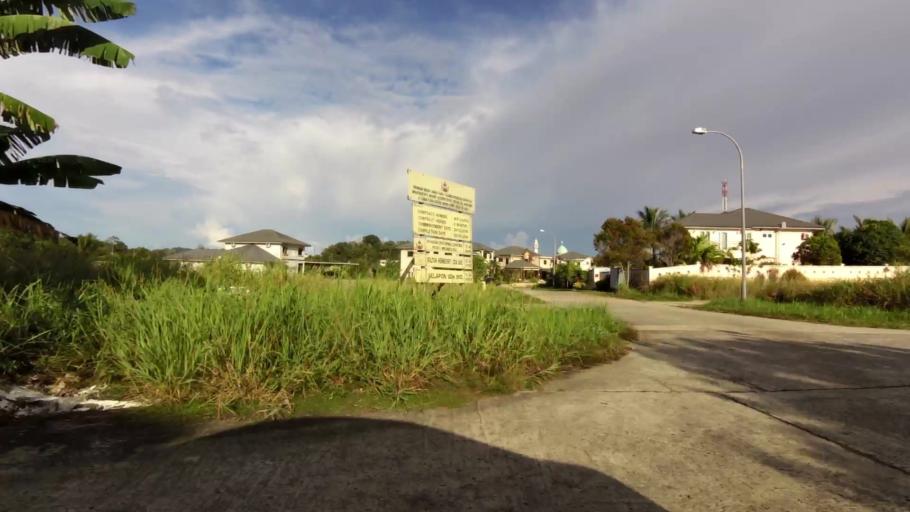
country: BN
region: Brunei and Muara
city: Bandar Seri Begawan
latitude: 4.9785
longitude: 114.9759
